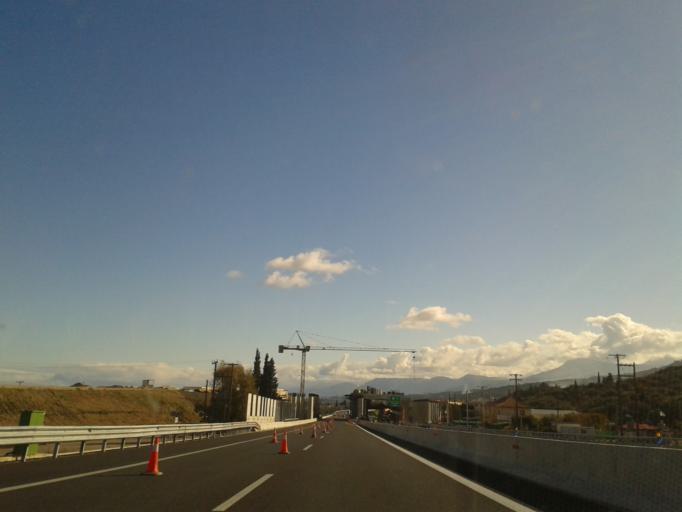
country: GR
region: West Greece
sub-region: Nomos Achaias
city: Kamarai
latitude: 38.2935
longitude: 22.0100
